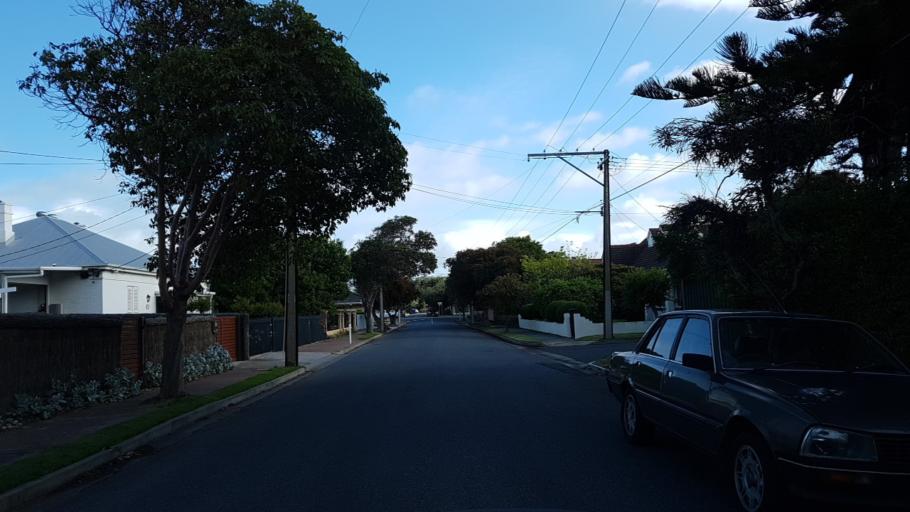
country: AU
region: South Australia
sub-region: Holdfast Bay
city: North Brighton
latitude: -34.9981
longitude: 138.5153
